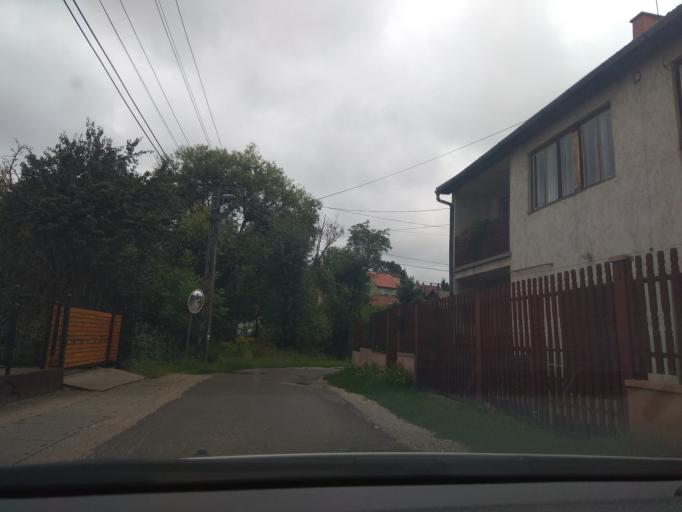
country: HU
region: Borsod-Abauj-Zemplen
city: Miskolc
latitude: 48.0541
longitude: 20.7758
